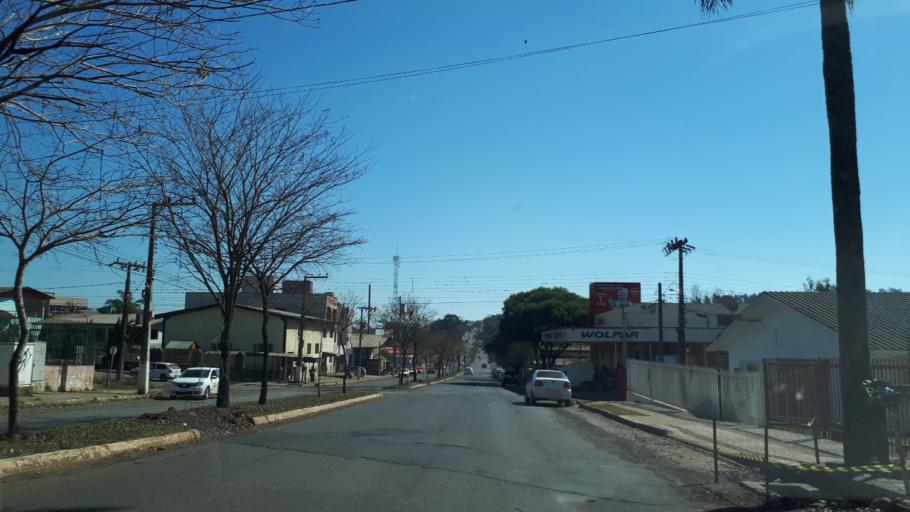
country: BR
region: Santa Catarina
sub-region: Chapeco
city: Chapeco
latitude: -27.1329
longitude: -52.6014
